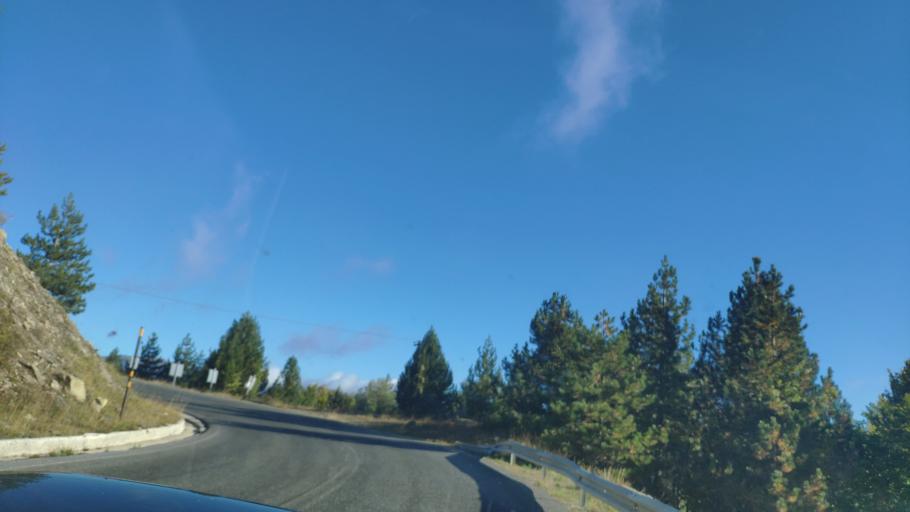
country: GR
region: Epirus
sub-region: Nomos Ioanninon
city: Metsovo
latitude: 39.7790
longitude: 21.1706
